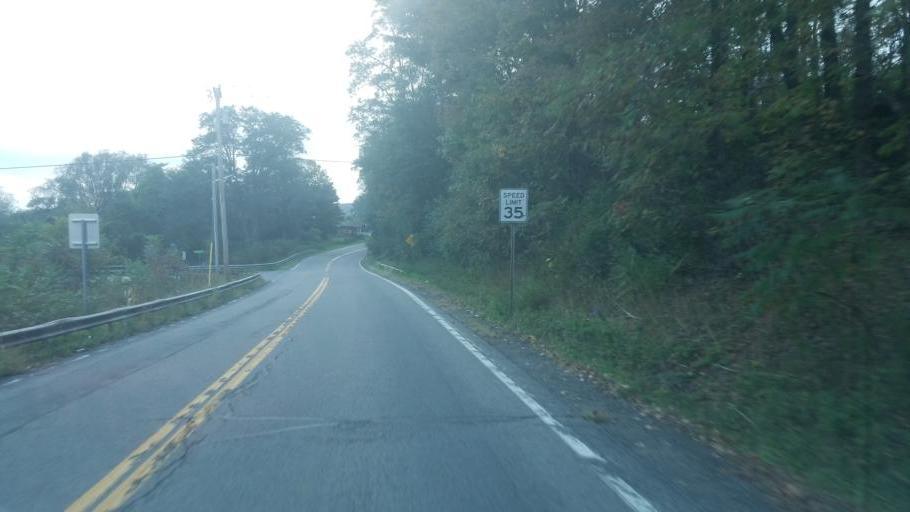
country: US
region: New York
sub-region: Cattaraugus County
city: Weston Mills
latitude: 42.1803
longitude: -78.3728
